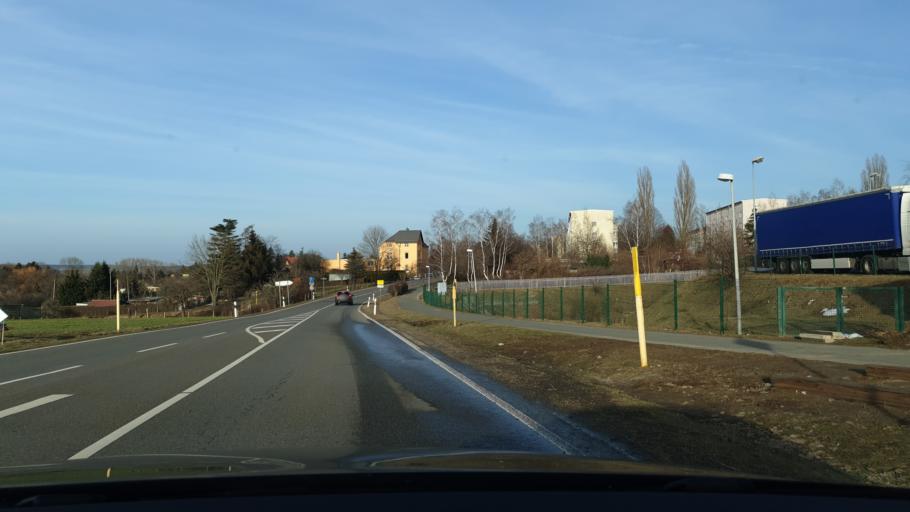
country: DE
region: Thuringia
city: Langenwolschendorf
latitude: 50.6432
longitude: 11.9685
